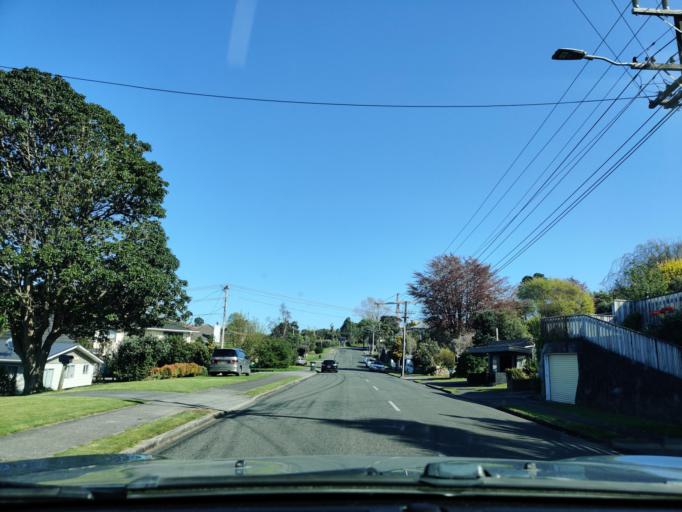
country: NZ
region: Taranaki
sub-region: New Plymouth District
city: New Plymouth
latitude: -39.0658
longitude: 174.0544
